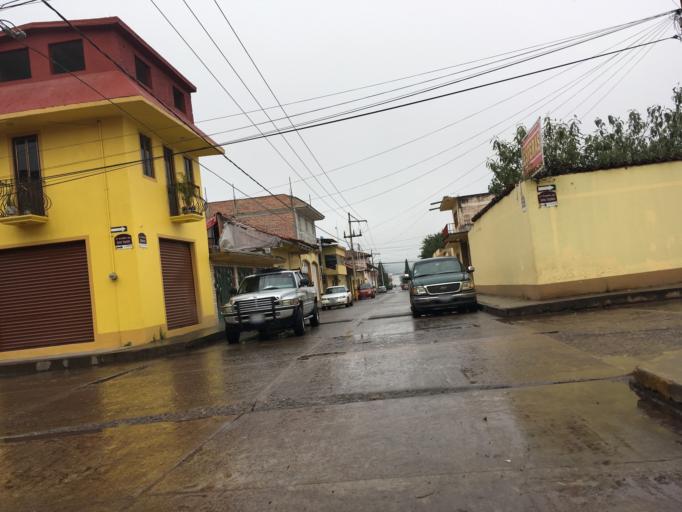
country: MX
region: Puebla
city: Chignahuapan
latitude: 19.8394
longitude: -98.0338
